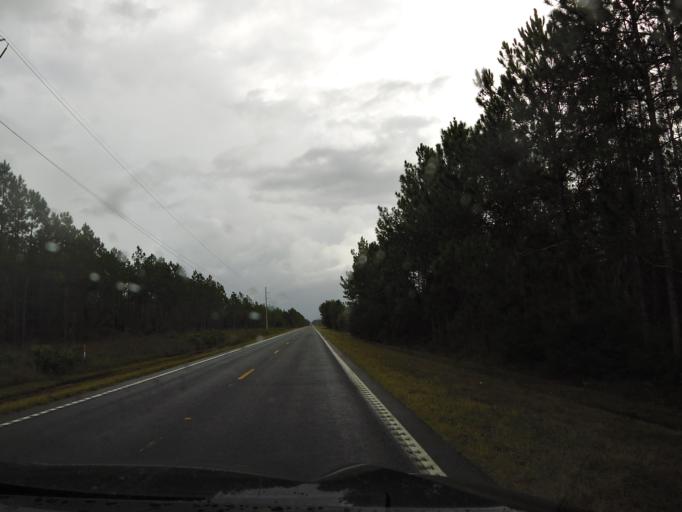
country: US
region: Florida
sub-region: Baker County
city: Macclenny
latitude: 30.4330
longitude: -82.0883
